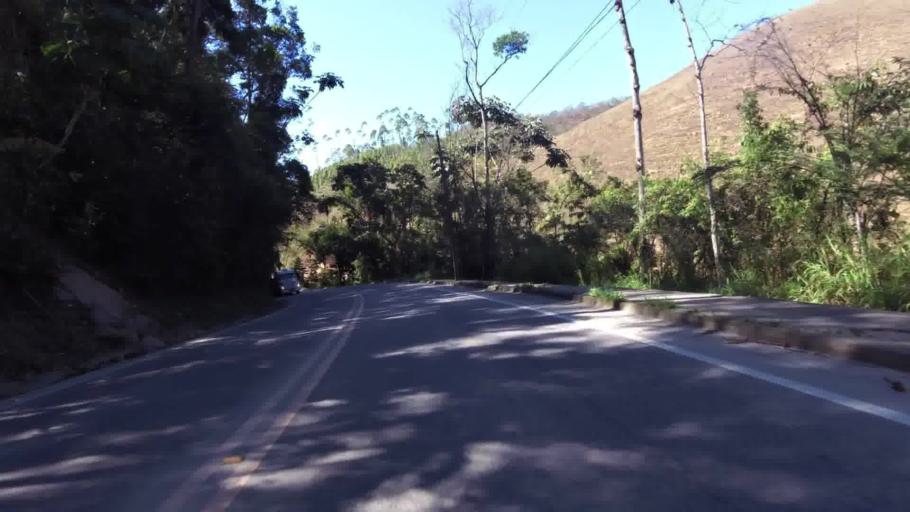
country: BR
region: Espirito Santo
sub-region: Vargem Alta
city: Vargem Alta
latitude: -20.6793
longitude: -41.0209
